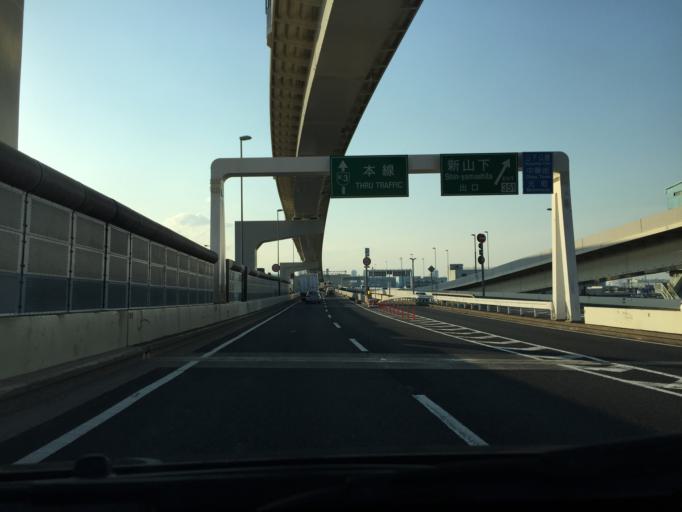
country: JP
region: Kanagawa
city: Yokohama
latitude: 35.4380
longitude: 139.6634
